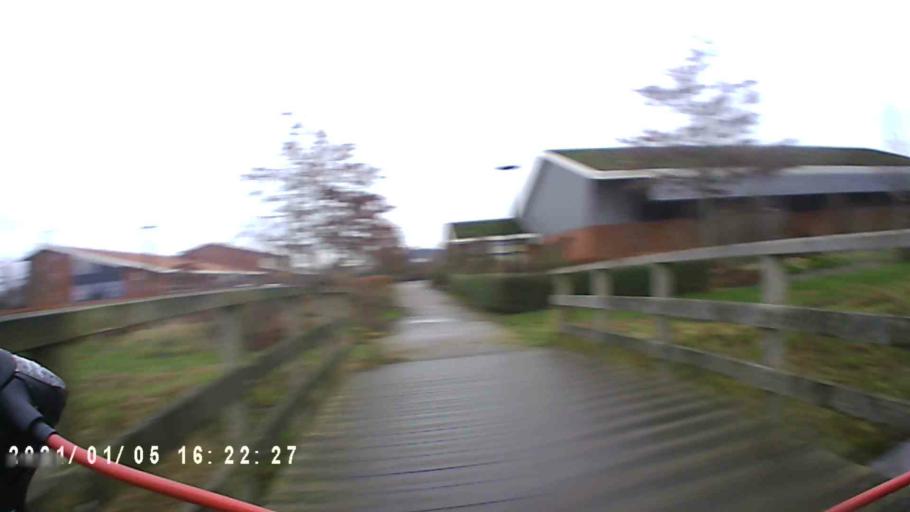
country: NL
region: Groningen
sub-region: Gemeente  Oldambt
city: Winschoten
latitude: 53.1988
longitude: 7.0389
